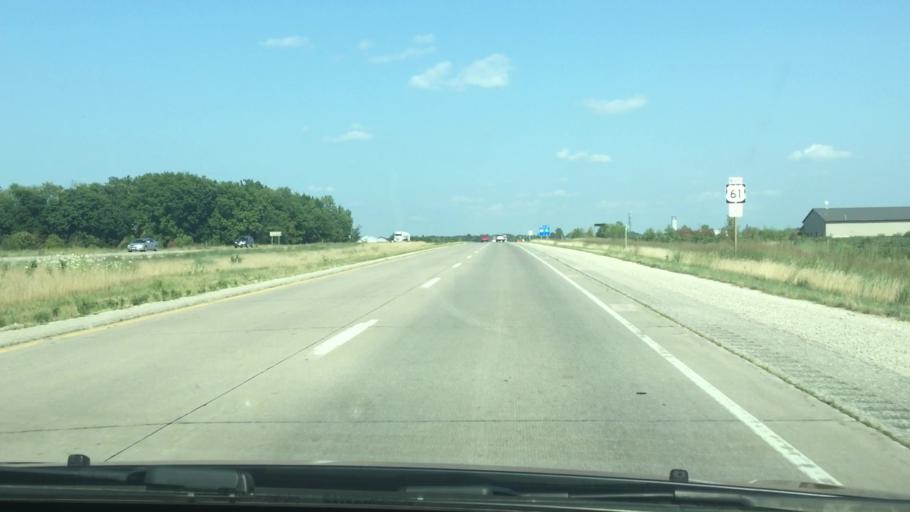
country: US
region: Iowa
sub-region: Scott County
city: Blue Grass
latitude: 41.5126
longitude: -90.7926
